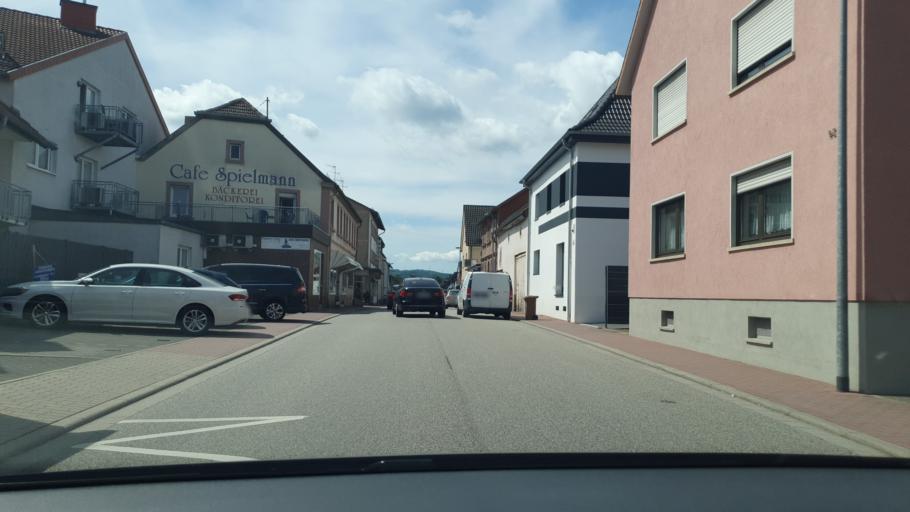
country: DE
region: Rheinland-Pfalz
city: Ramstein-Miesenbach
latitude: 49.4432
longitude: 7.5567
